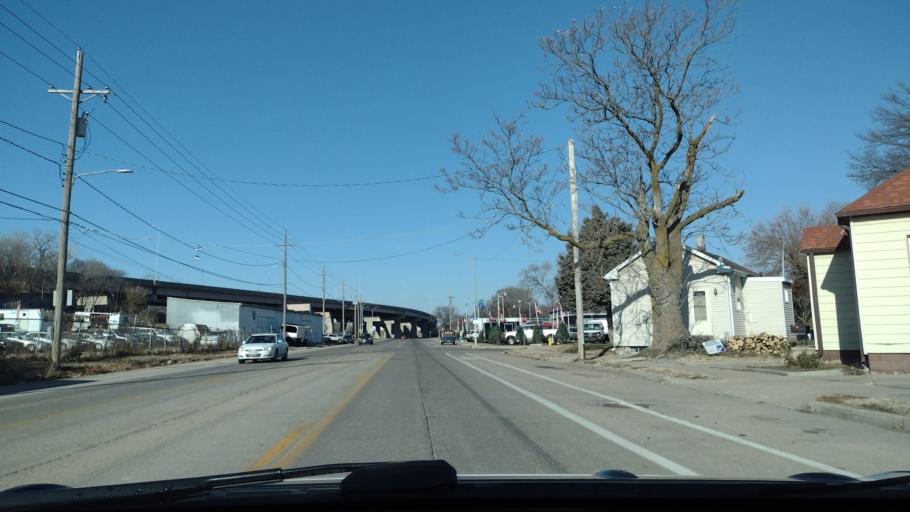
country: US
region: Nebraska
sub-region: Douglas County
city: Omaha
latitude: 41.1934
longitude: -95.9392
